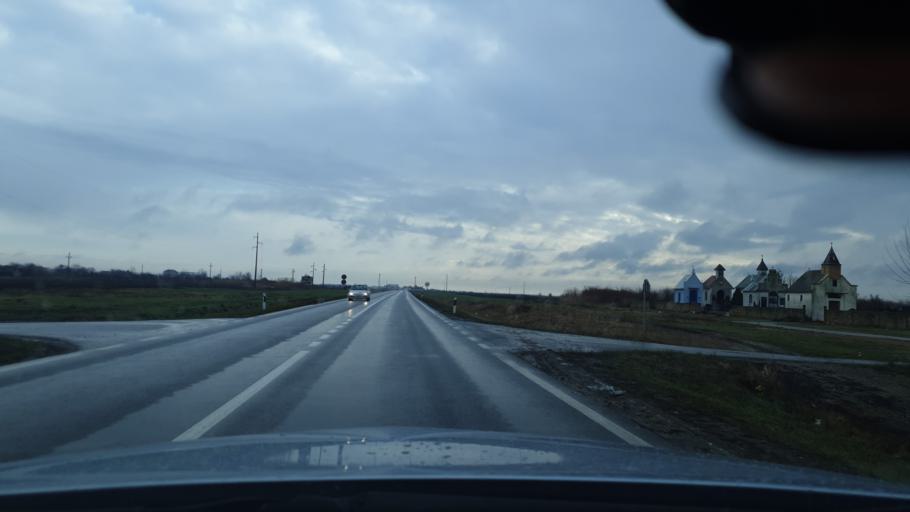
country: RS
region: Autonomna Pokrajina Vojvodina
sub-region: Juznobanatski Okrug
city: Kovin
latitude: 44.8090
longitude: 20.8694
